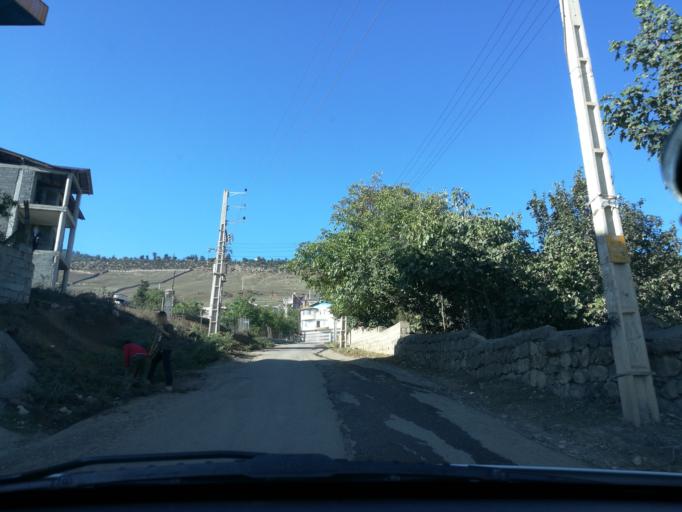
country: IR
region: Mazandaran
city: `Abbasabad
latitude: 36.5553
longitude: 51.1933
